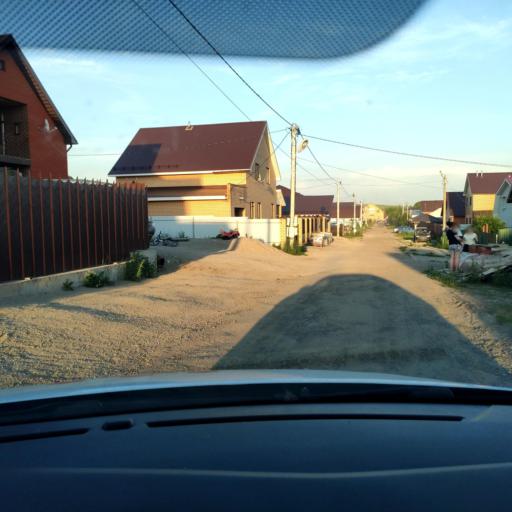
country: RU
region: Tatarstan
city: Stolbishchi
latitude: 55.7514
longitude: 49.3042
